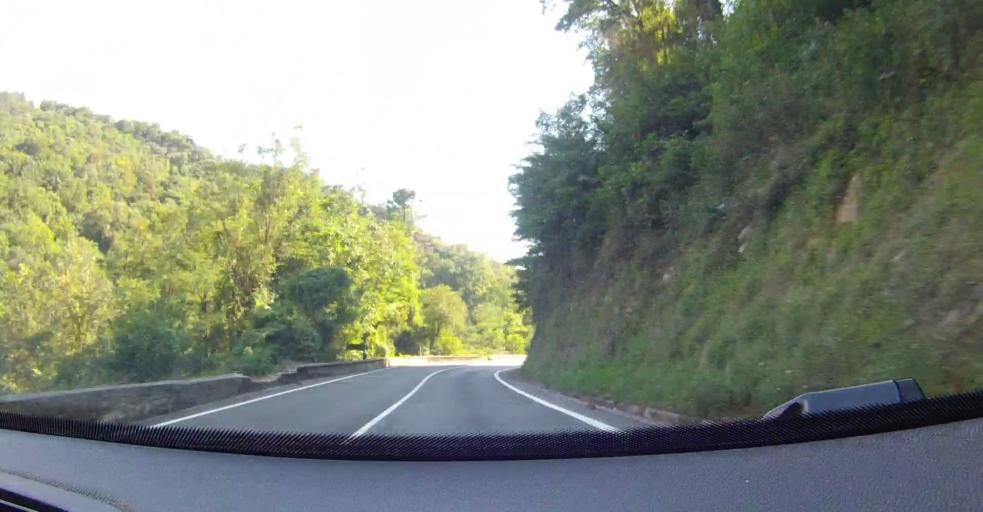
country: ES
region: Basque Country
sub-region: Bizkaia
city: Muxika
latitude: 43.2602
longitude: -2.6893
